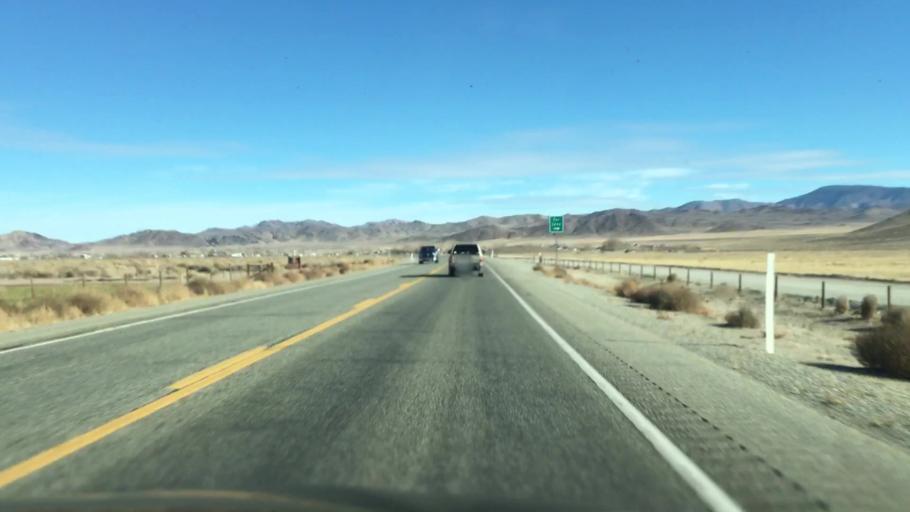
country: US
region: Nevada
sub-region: Lyon County
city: Yerington
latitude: 38.9975
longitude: -119.1082
